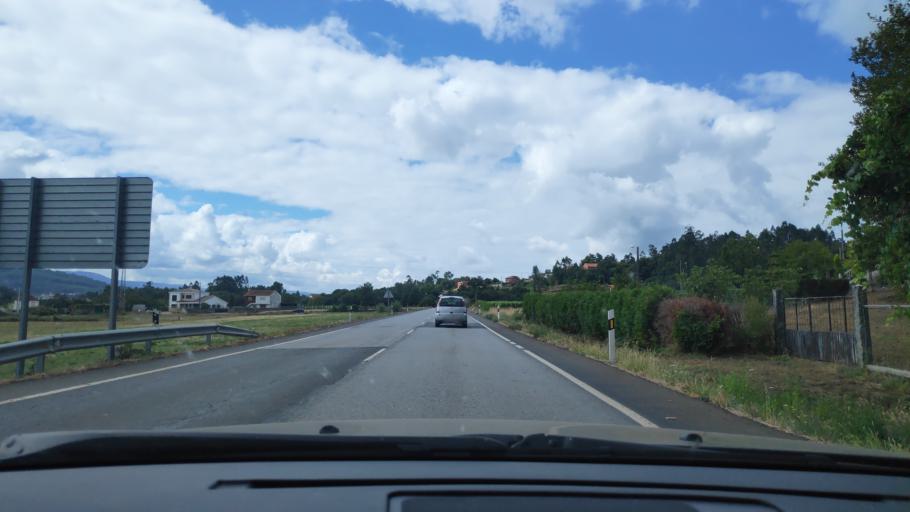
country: ES
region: Galicia
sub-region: Provincia de Pontevedra
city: Portas
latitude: 42.5942
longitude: -8.6885
